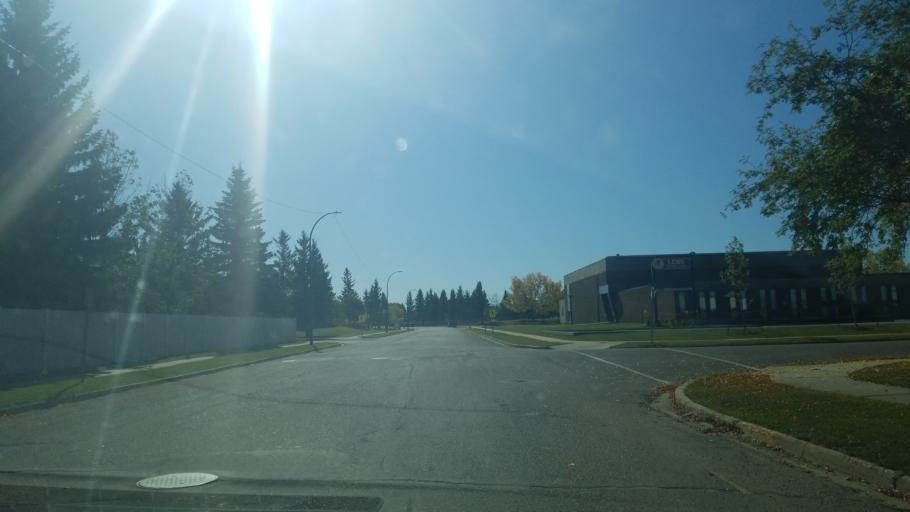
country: CA
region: Saskatchewan
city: Lloydminster
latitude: 53.2762
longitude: -110.0198
